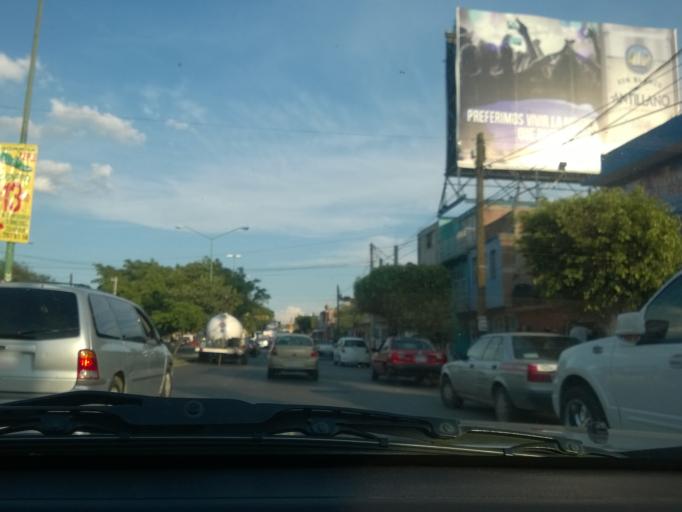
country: MX
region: Guanajuato
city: Leon
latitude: 21.1319
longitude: -101.6688
